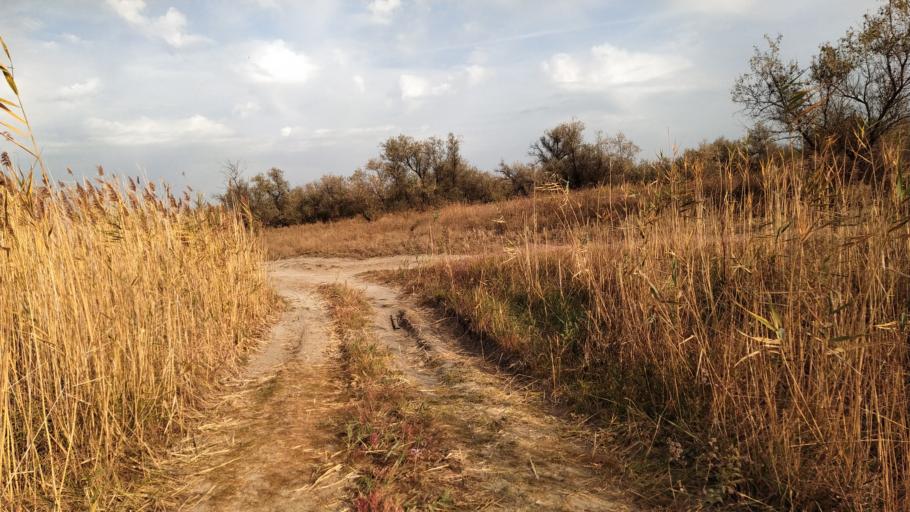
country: RU
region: Rostov
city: Kuleshovka
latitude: 47.1390
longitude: 39.5821
